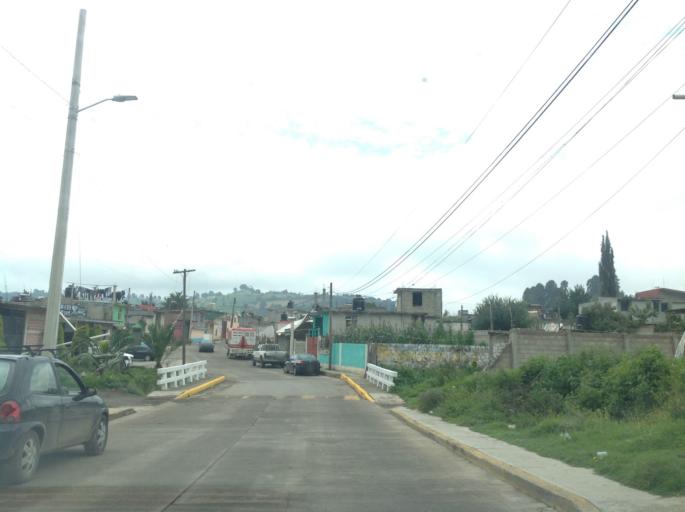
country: MX
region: Morelos
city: Joquicingo de Leon Guzman
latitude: 19.0535
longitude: -99.5337
